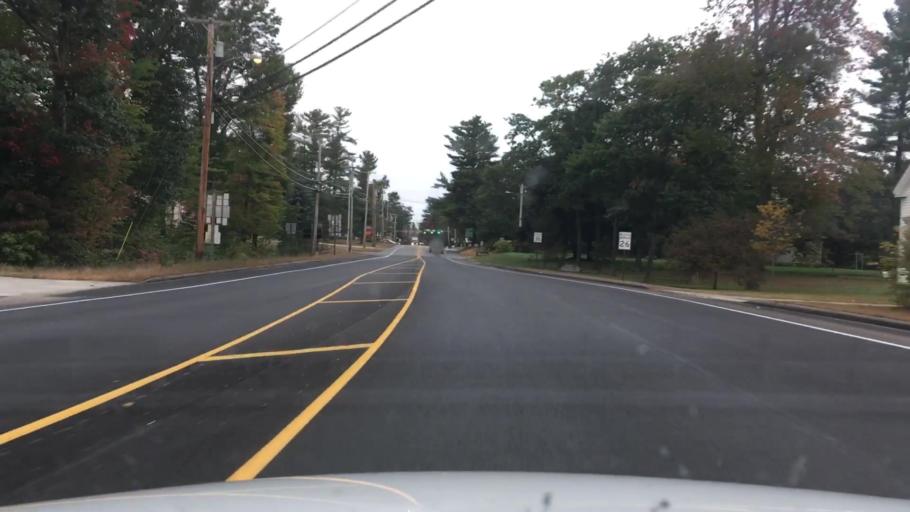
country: US
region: Maine
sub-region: Cumberland County
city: New Gloucester
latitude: 43.8998
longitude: -70.3435
